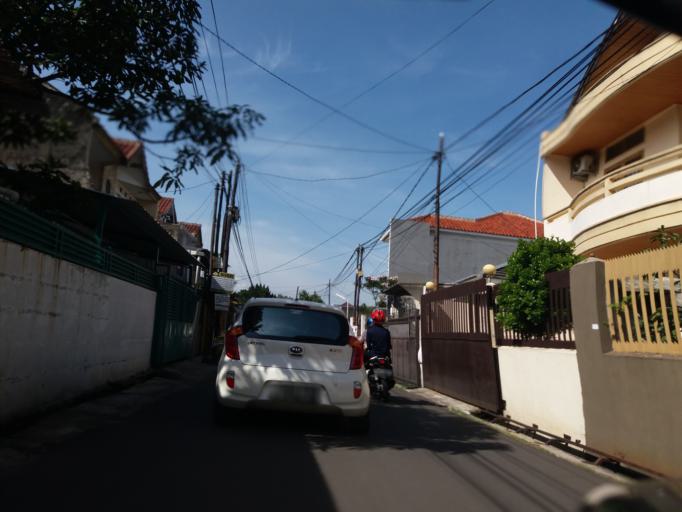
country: ID
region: West Java
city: Bandung
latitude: -6.9437
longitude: 107.6103
